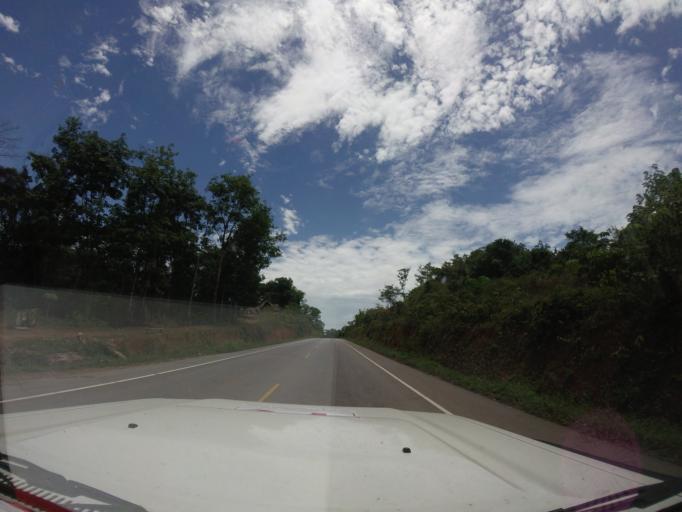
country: LR
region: Bong
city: Gbarnga
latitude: 6.8143
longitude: -9.9138
